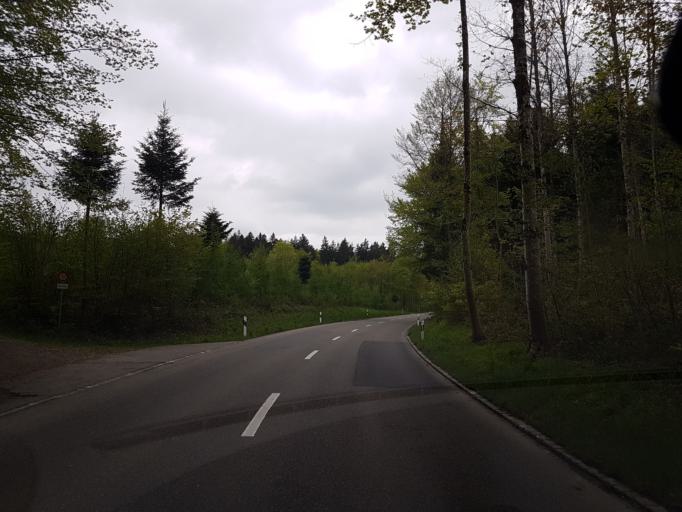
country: CH
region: Zurich
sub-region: Bezirk Dietikon
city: Birmensdorf
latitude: 47.3653
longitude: 8.4461
